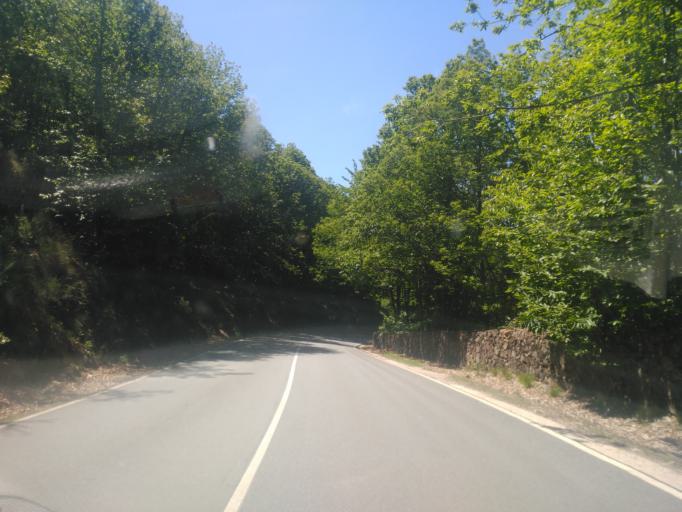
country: ES
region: Castille and Leon
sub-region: Provincia de Salamanca
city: Candelario
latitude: 40.3804
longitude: -5.7496
